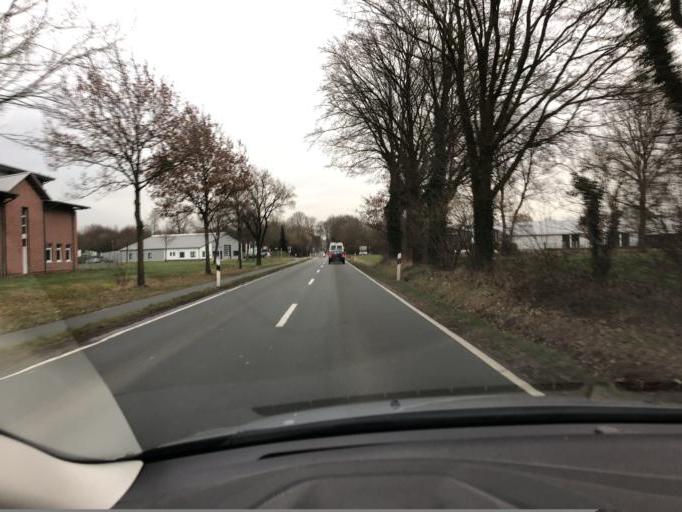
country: DE
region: Lower Saxony
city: Wiefelstede
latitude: 53.1873
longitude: 8.1173
